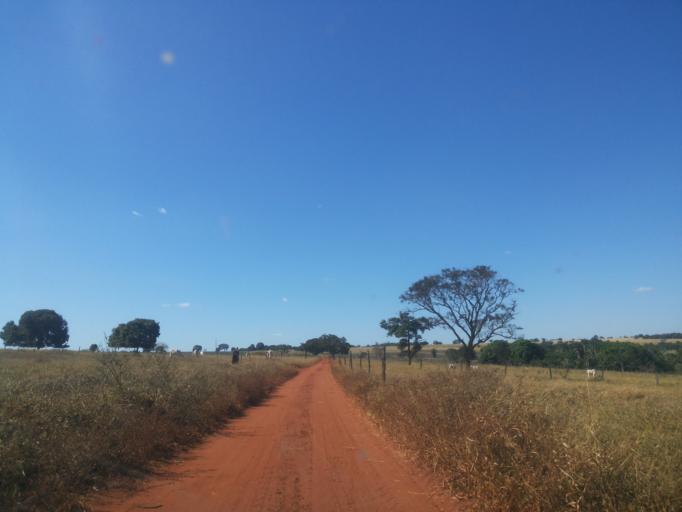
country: BR
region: Minas Gerais
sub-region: Centralina
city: Centralina
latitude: -18.7537
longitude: -49.1875
